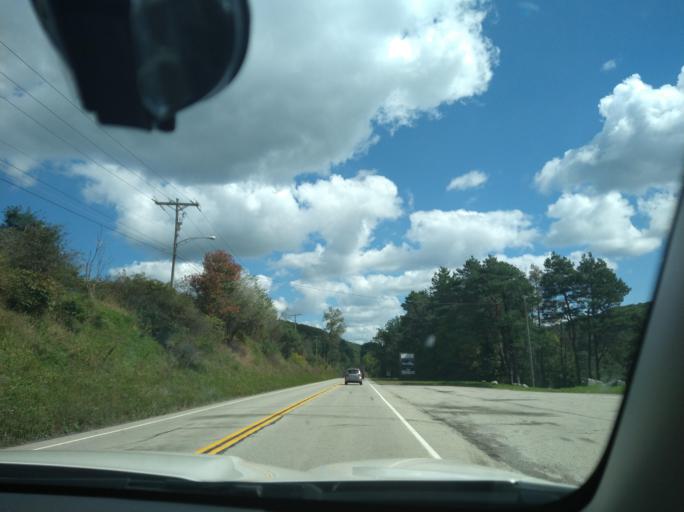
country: US
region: Pennsylvania
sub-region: Westmoreland County
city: Ligonier
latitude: 40.0662
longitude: -79.2460
